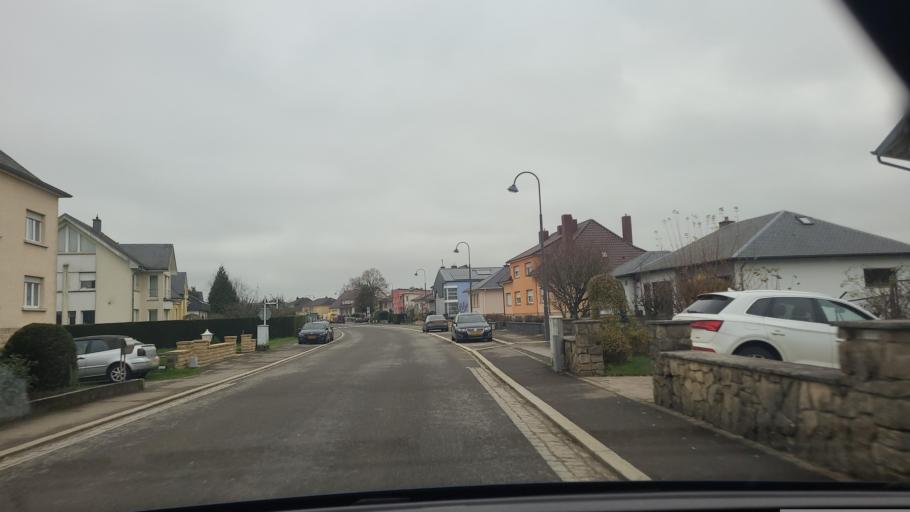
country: LU
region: Luxembourg
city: Schouweiler
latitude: 49.5862
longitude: 5.9553
